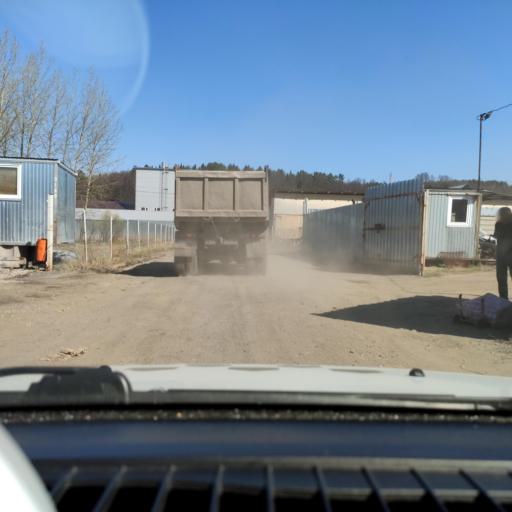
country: RU
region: Perm
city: Perm
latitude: 58.0699
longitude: 56.3695
